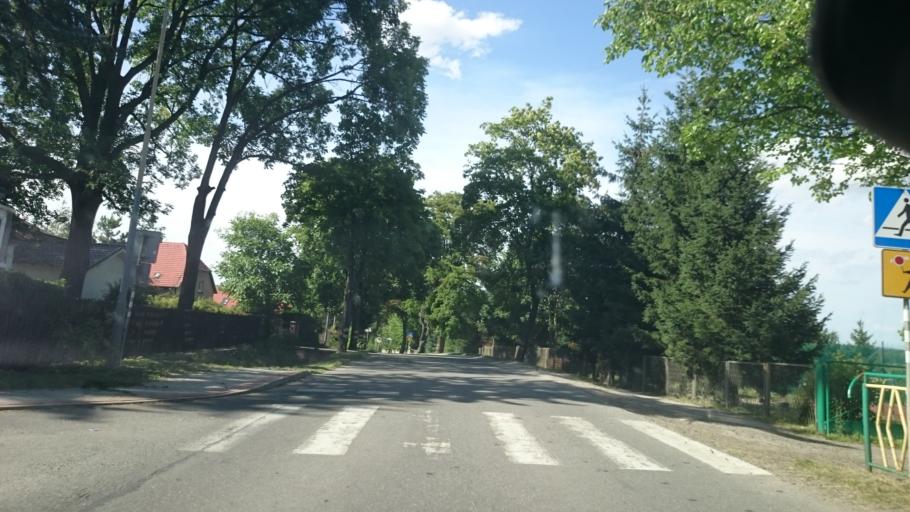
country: PL
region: Lower Silesian Voivodeship
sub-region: Powiat klodzki
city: Polanica-Zdroj
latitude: 50.3939
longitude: 16.5218
